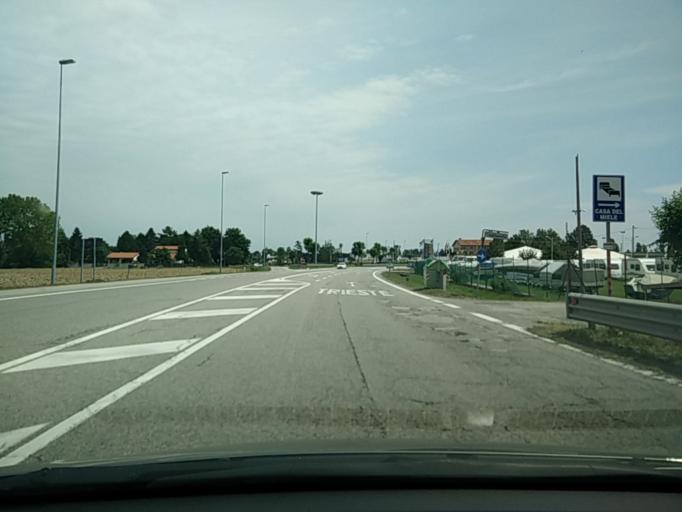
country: IT
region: Veneto
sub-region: Provincia di Venezia
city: Tessera
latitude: 45.5176
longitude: 12.3553
